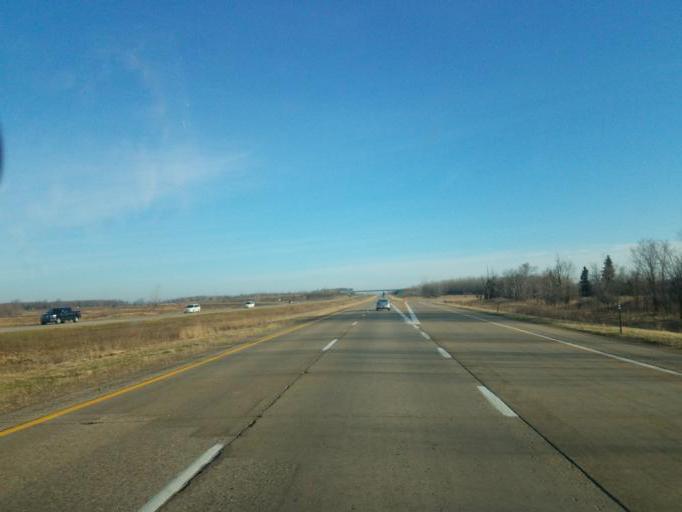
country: US
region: Michigan
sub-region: Clinton County
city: Saint Johns
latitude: 42.9213
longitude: -84.5187
